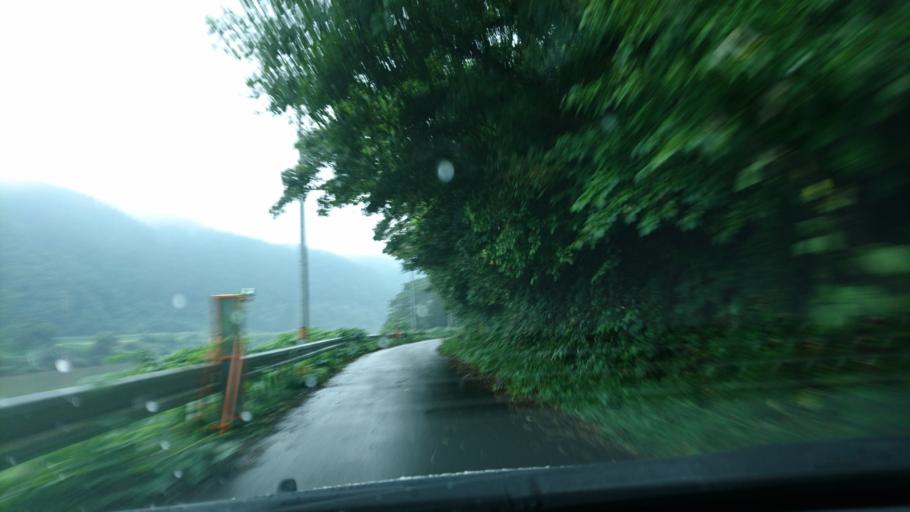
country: JP
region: Iwate
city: Ichinoseki
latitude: 38.8705
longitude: 141.2611
